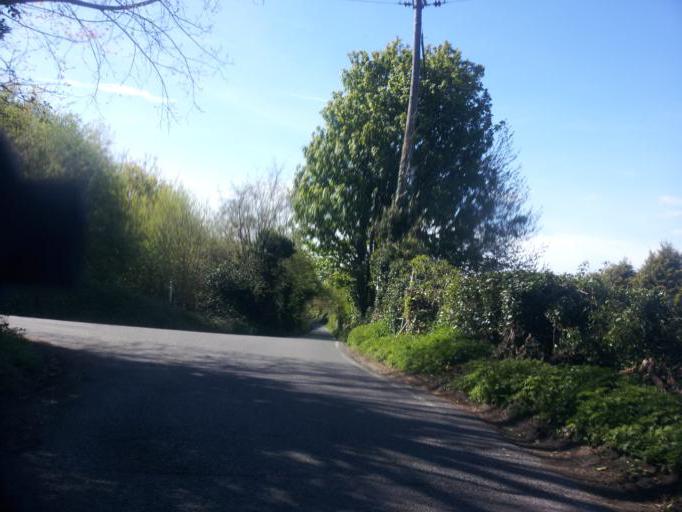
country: GB
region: England
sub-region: Kent
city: Rainham
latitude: 51.3667
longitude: 0.6337
